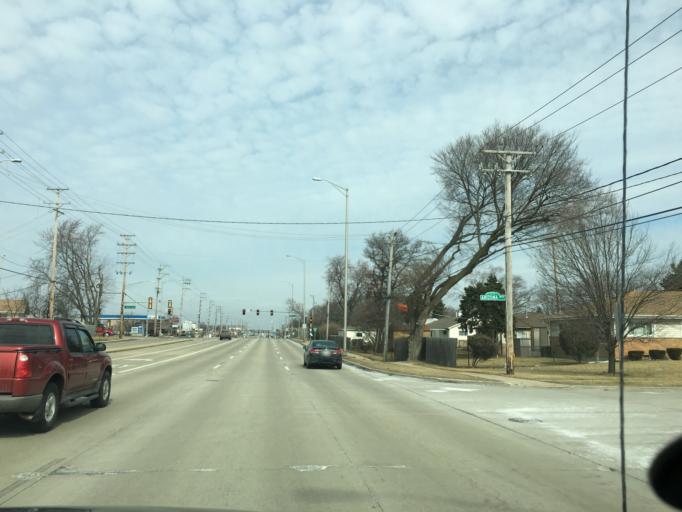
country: US
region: Illinois
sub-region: Cook County
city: Hoffman Estates
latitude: 42.0416
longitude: -88.0796
